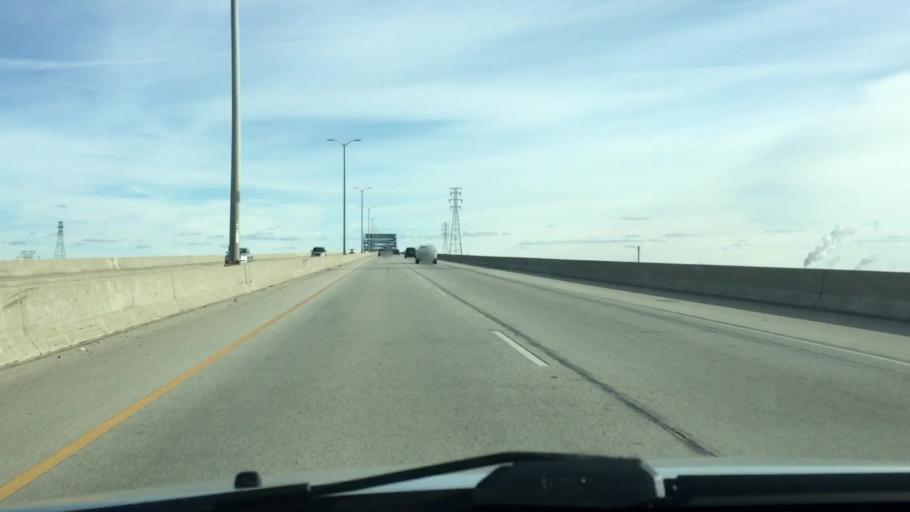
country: US
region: Wisconsin
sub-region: Brown County
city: Green Bay
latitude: 44.5362
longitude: -88.0172
